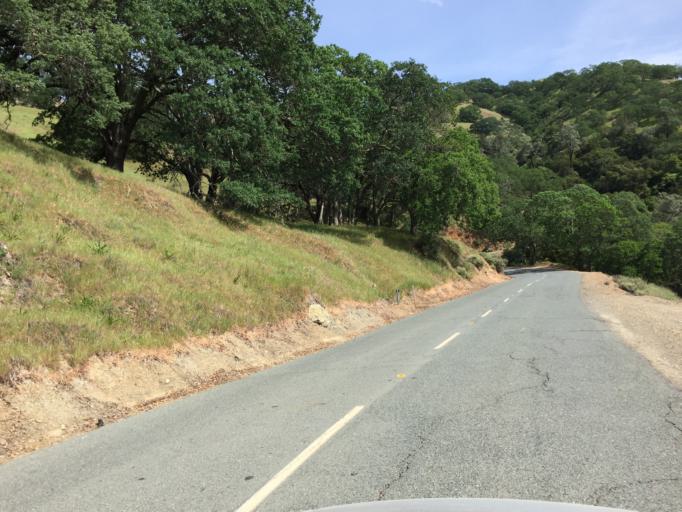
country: US
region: California
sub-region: Contra Costa County
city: Diablo
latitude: 37.8729
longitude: -121.9525
